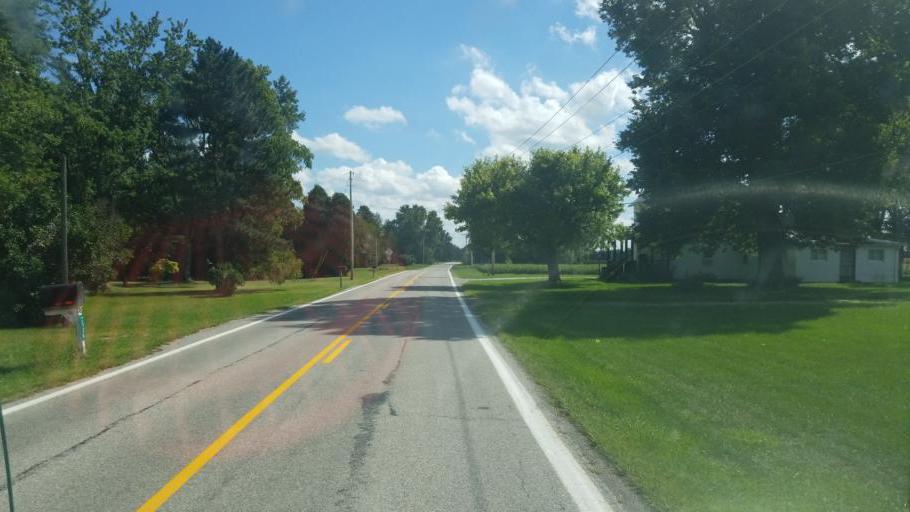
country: US
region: Ohio
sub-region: Marion County
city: Prospect
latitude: 40.3620
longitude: -83.1854
